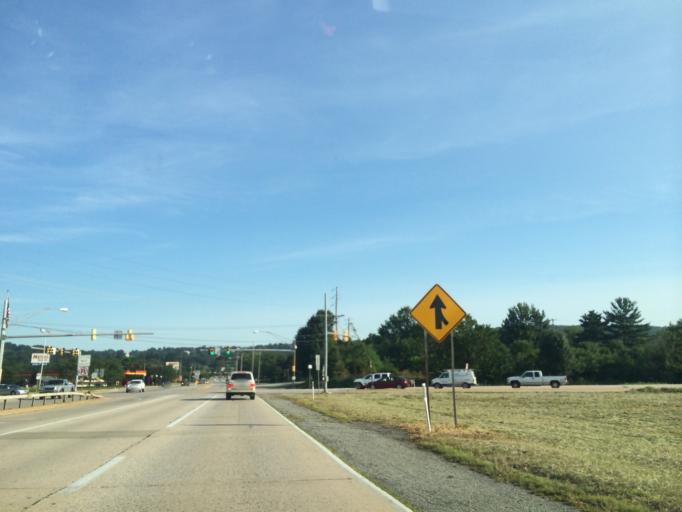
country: US
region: Pennsylvania
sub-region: York County
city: Yorklyn
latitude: 39.9875
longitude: -76.6681
